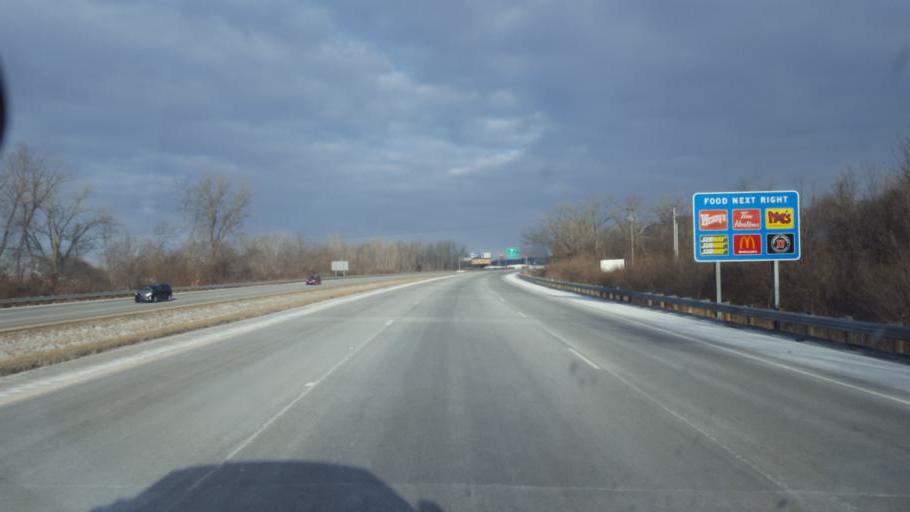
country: US
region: Ohio
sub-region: Ross County
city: Chillicothe
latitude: 39.3270
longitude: -82.9448
